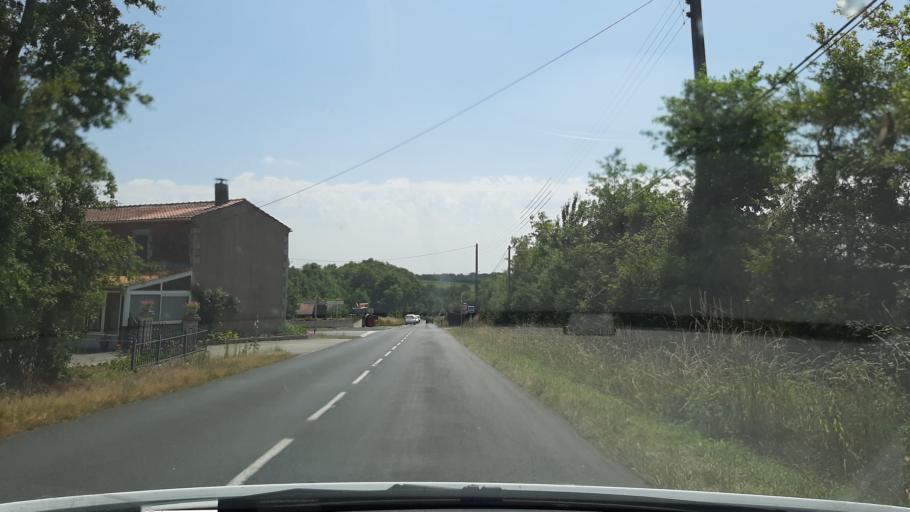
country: FR
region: Pays de la Loire
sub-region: Departement de la Vendee
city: Le Poire-sur-Vie
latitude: 46.7836
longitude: -1.5392
